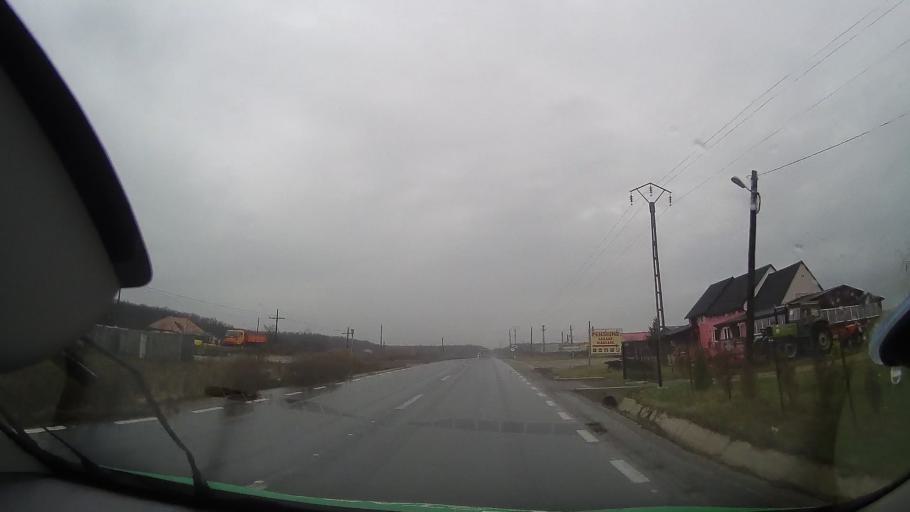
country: RO
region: Bihor
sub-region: Comuna Olcea
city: Olcea
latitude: 46.6880
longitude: 21.9659
